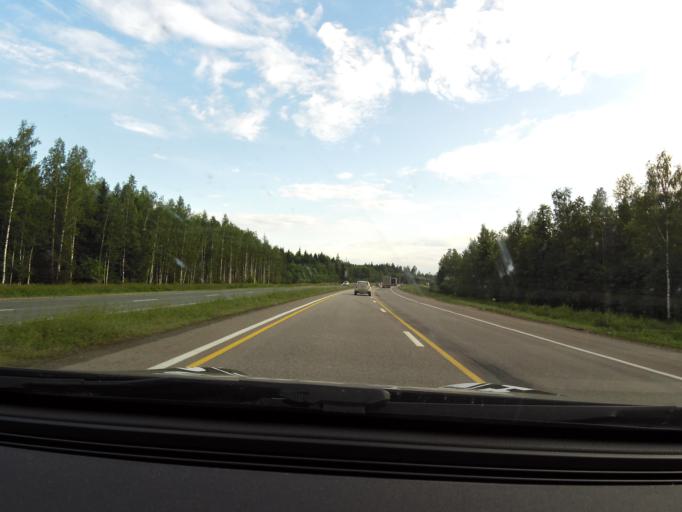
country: RU
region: Vladimir
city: Kameshkovo
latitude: 56.1787
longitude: 40.9464
